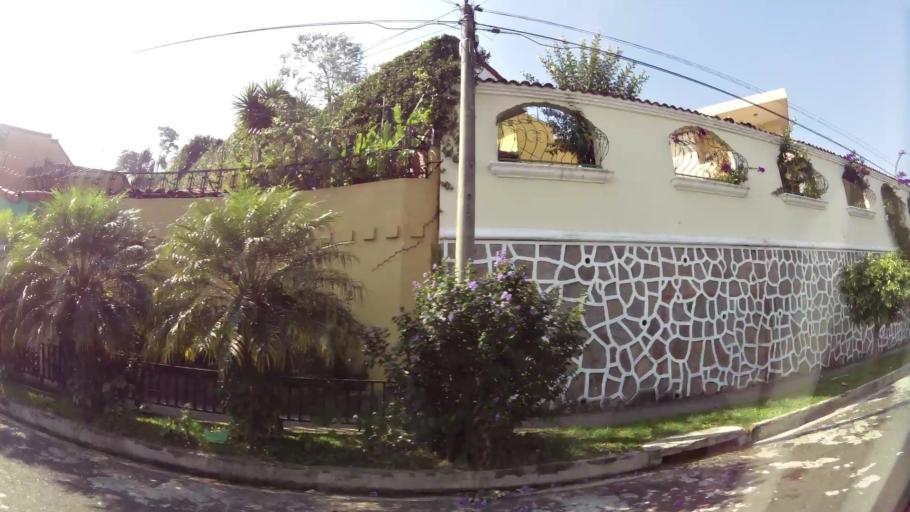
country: SV
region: La Libertad
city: Antiguo Cuscatlan
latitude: 13.6683
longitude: -89.2305
